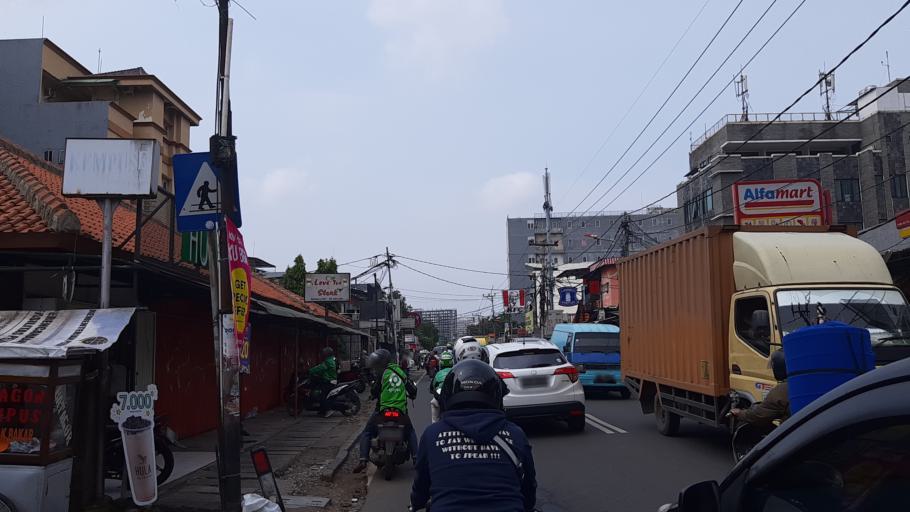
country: ID
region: Jakarta Raya
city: Jakarta
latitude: -6.2013
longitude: 106.7829
